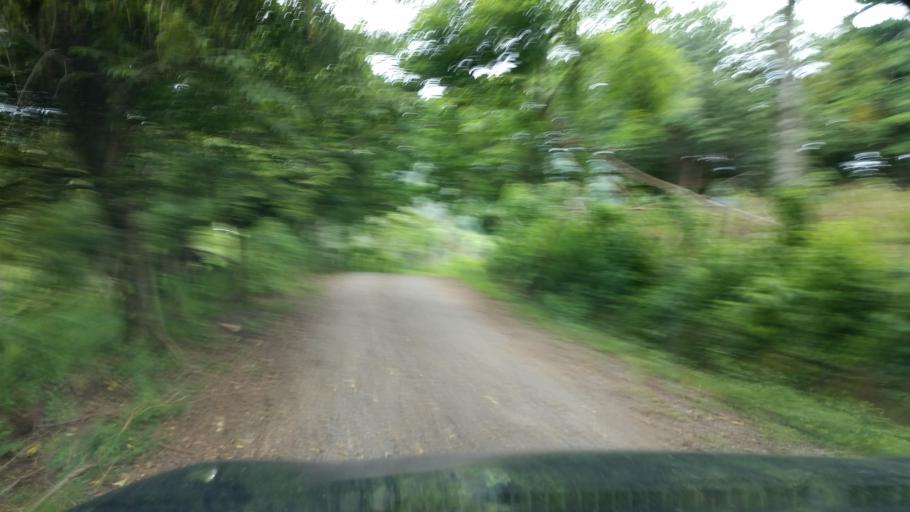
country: NI
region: Atlantico Norte (RAAN)
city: Waslala
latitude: 13.2652
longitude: -85.6203
